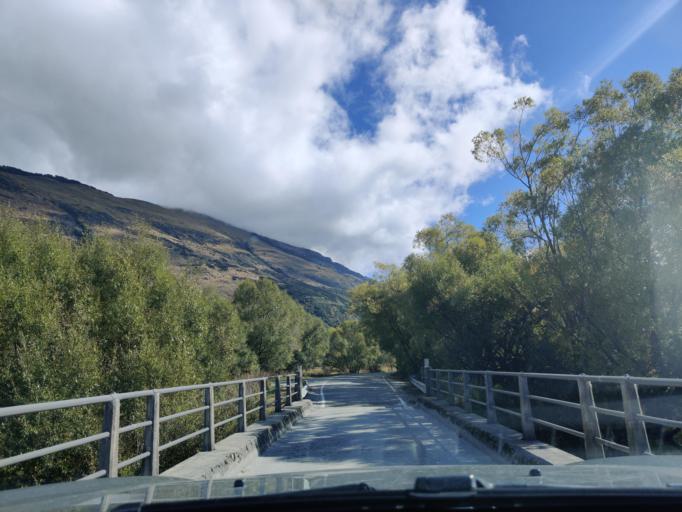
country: NZ
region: Otago
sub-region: Queenstown-Lakes District
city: Queenstown
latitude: -44.7866
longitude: 168.3961
